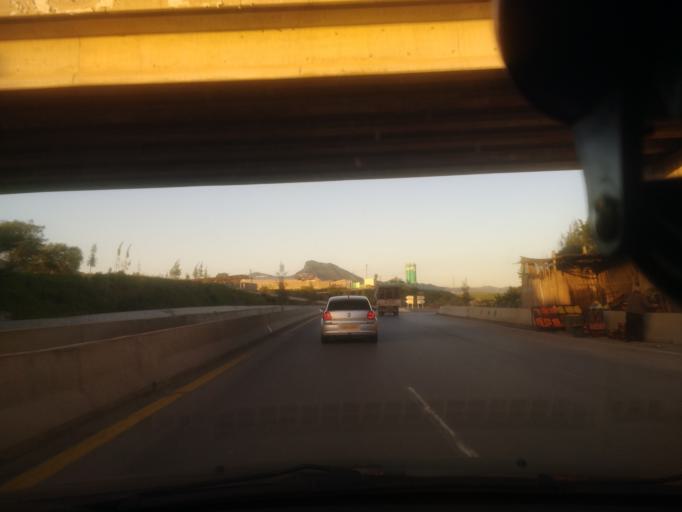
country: DZ
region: Tizi Ouzou
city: Tizi Ouzou
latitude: 36.7529
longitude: 4.0327
